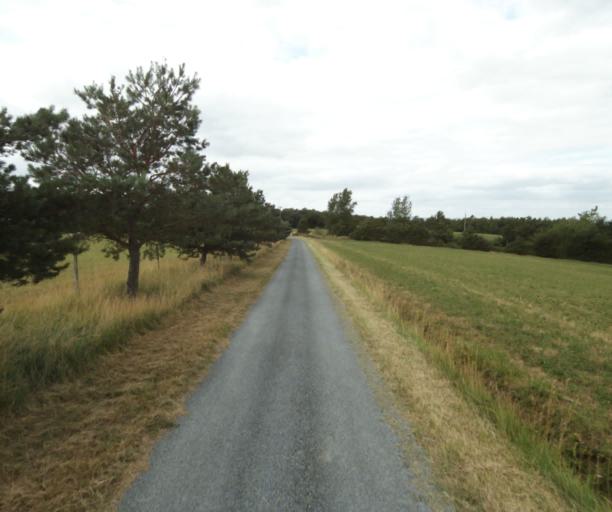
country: FR
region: Midi-Pyrenees
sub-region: Departement du Tarn
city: Soreze
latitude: 43.4631
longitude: 2.0868
